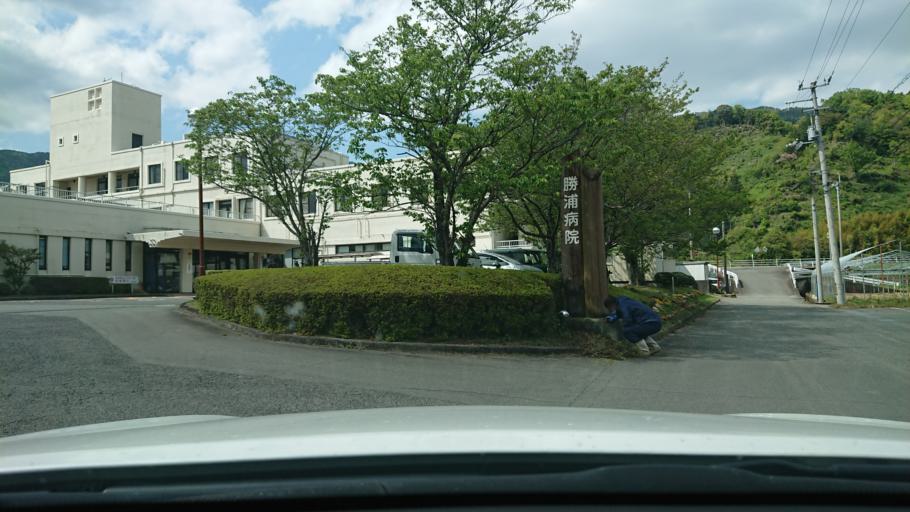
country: JP
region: Tokushima
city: Komatsushimacho
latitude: 33.9328
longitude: 134.5057
